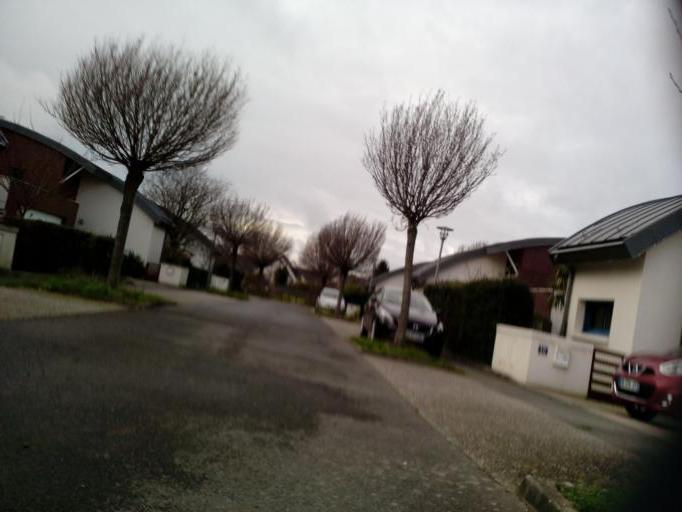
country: FR
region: Brittany
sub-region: Departement d'Ille-et-Vilaine
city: Chantepie
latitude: 48.0942
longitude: -1.6410
